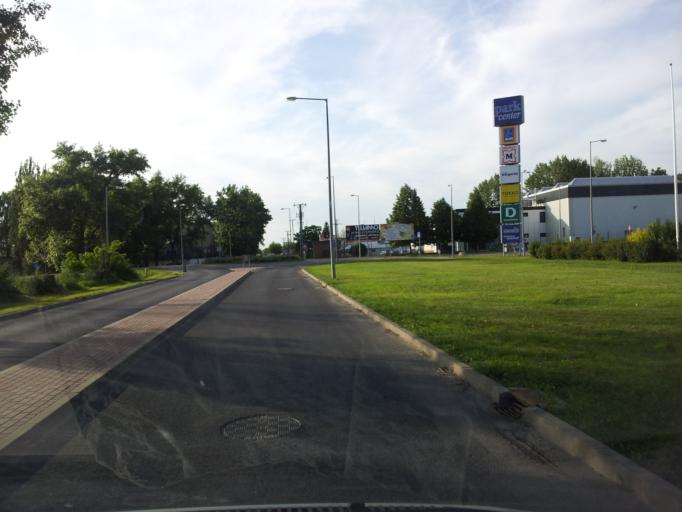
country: HU
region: Komarom-Esztergom
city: Esztergom
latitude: 47.7749
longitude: 18.7545
